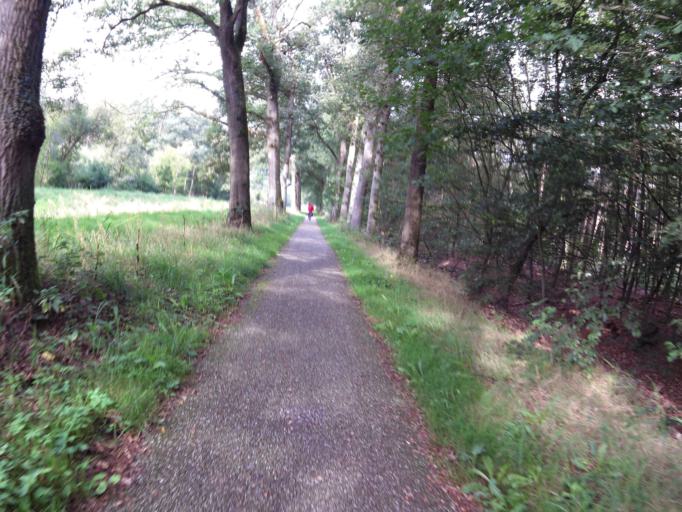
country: NL
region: Gelderland
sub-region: Oude IJsselstreek
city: Varsseveld
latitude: 51.9633
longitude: 6.4337
